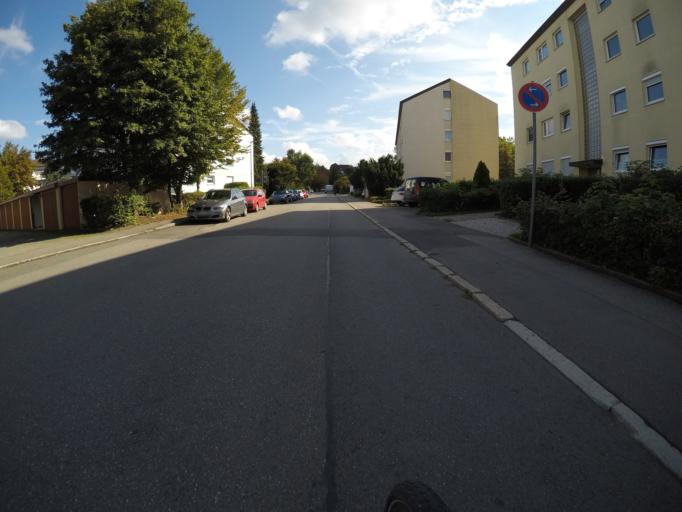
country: DE
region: Baden-Wuerttemberg
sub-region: Regierungsbezirk Stuttgart
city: Boeblingen
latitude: 48.6771
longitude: 8.9947
